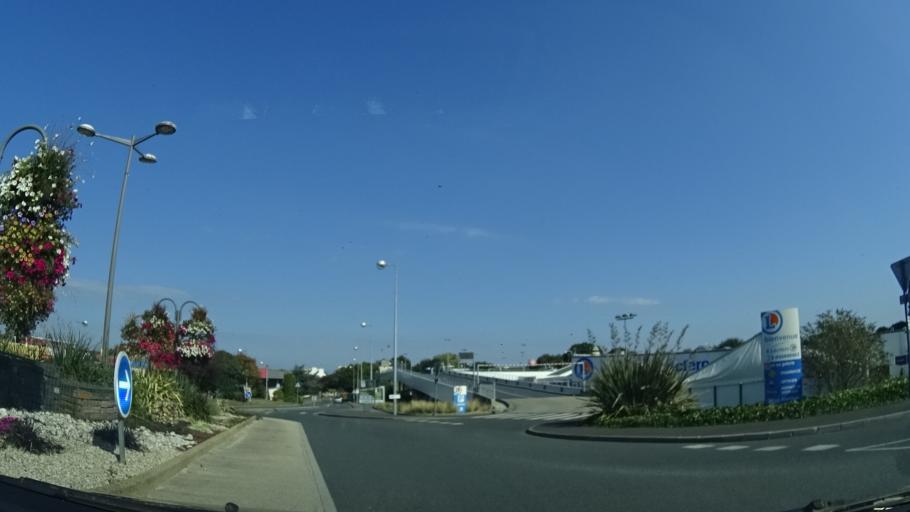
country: FR
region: Brittany
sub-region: Departement du Finistere
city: Douarnenez
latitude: 48.0908
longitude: -4.3464
